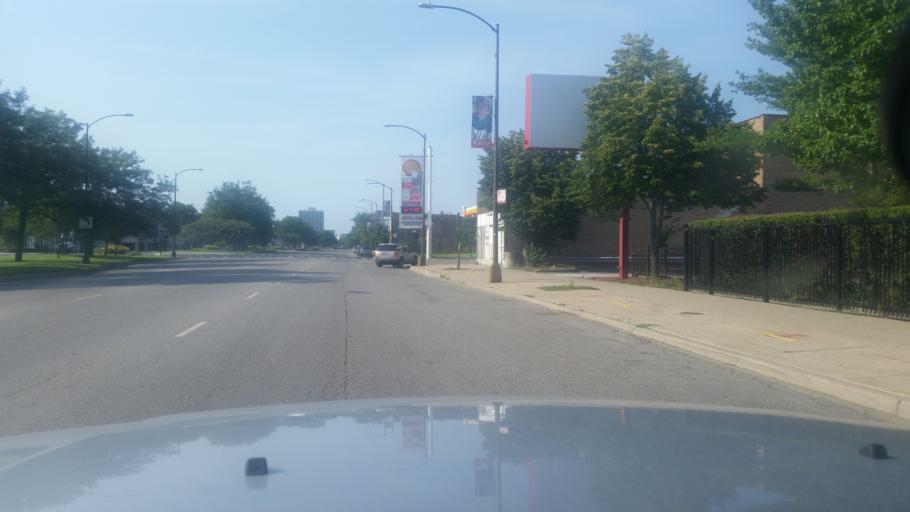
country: US
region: Illinois
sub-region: Cook County
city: Chicago
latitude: 41.7670
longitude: -87.5859
